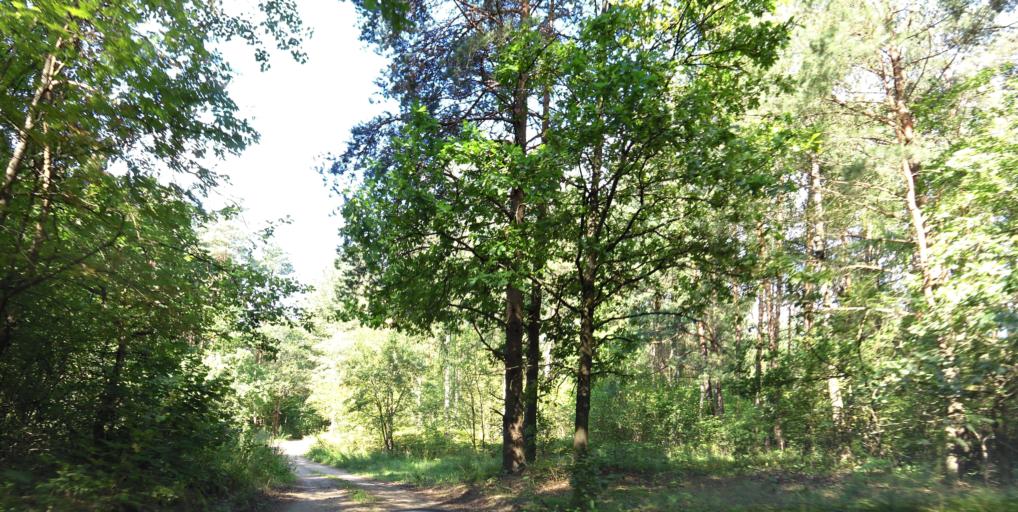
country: LT
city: Grigiskes
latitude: 54.7415
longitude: 25.0276
